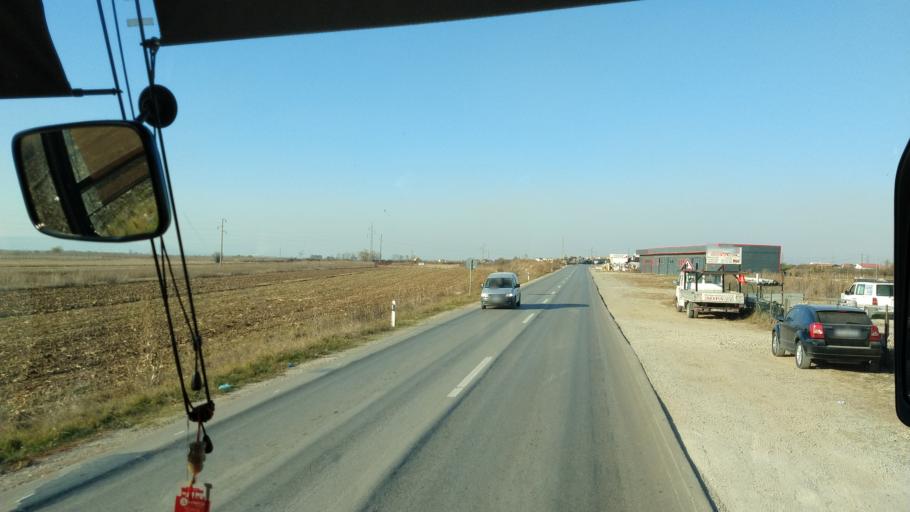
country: XK
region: Pristina
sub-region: Lipjan
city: Lipljan
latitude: 42.5230
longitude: 21.1122
